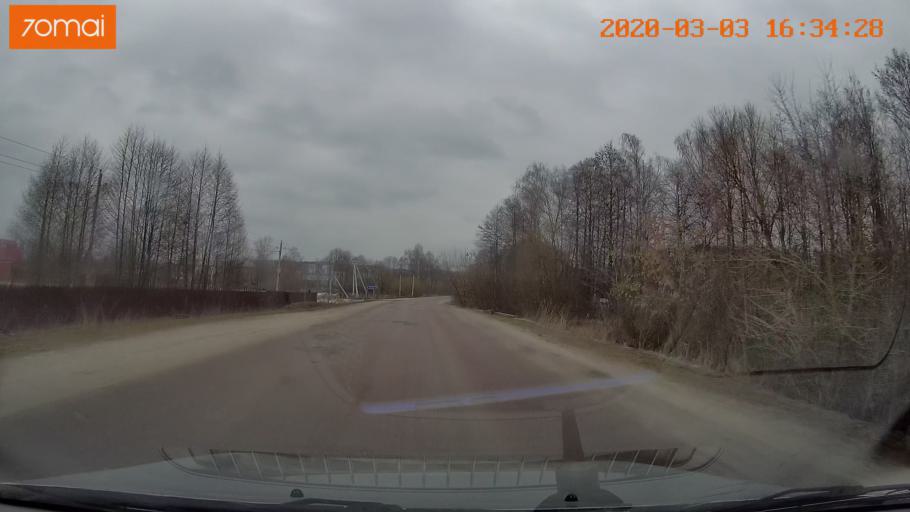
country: RU
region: Moskovskaya
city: Lopatinskiy
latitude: 55.4077
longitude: 38.7571
